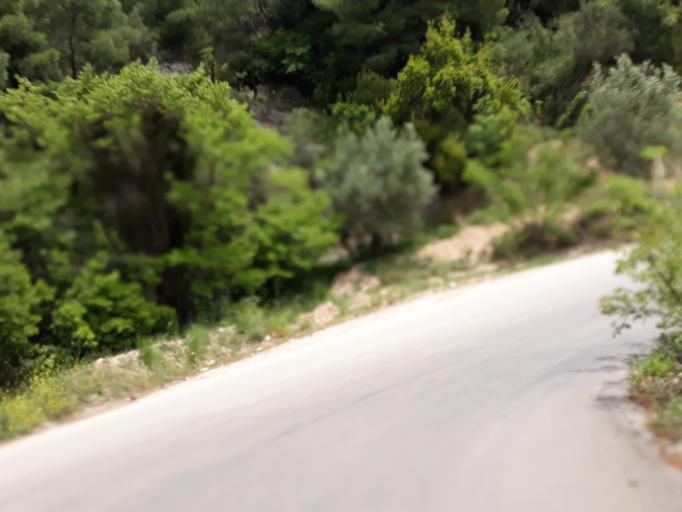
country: GR
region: Attica
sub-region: Nomarchia Dytikis Attikis
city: Magoula
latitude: 38.1502
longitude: 23.5209
